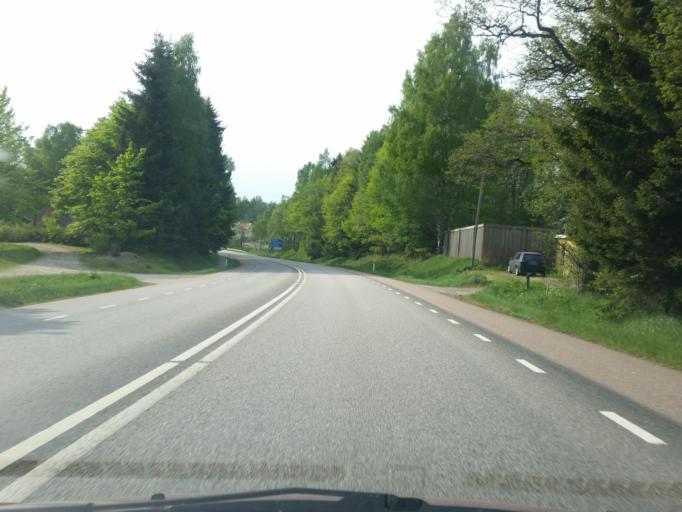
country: SE
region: Vaestra Goetaland
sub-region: Ulricehamns Kommun
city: Ulricehamn
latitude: 57.8117
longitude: 13.2949
